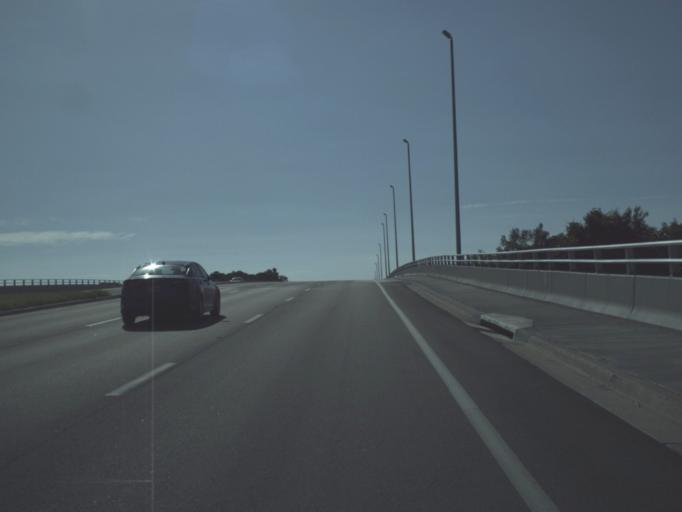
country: US
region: Florida
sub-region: Lee County
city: Fort Myers
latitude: 26.6133
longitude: -81.8567
